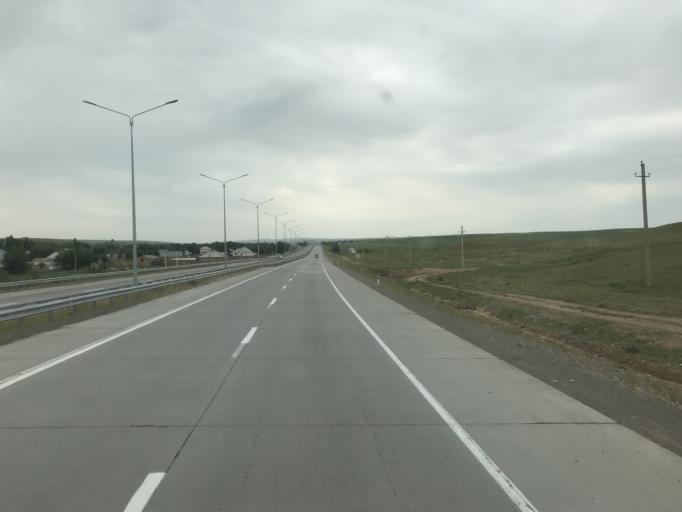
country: KZ
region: Ongtustik Qazaqstan
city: Qazyqurt
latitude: 41.8949
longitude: 69.4517
